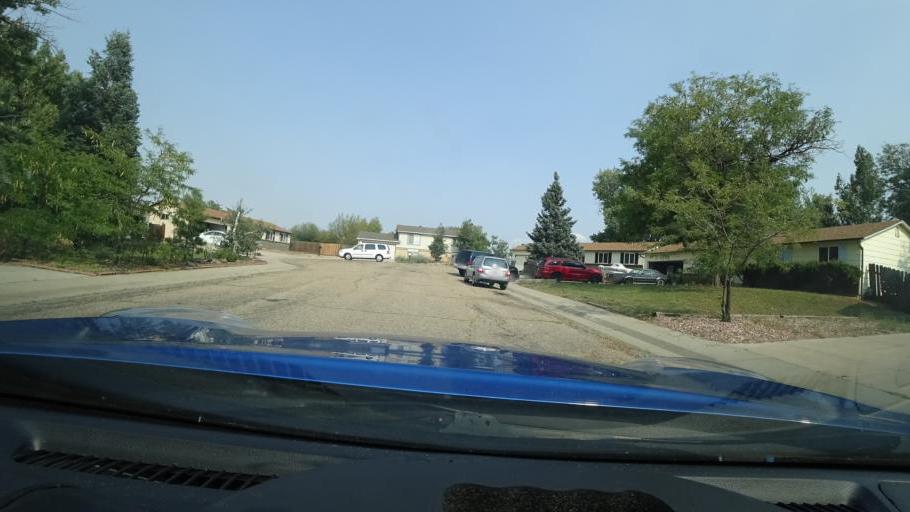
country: US
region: Colorado
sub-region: Adams County
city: Aurora
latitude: 39.6663
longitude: -104.8050
